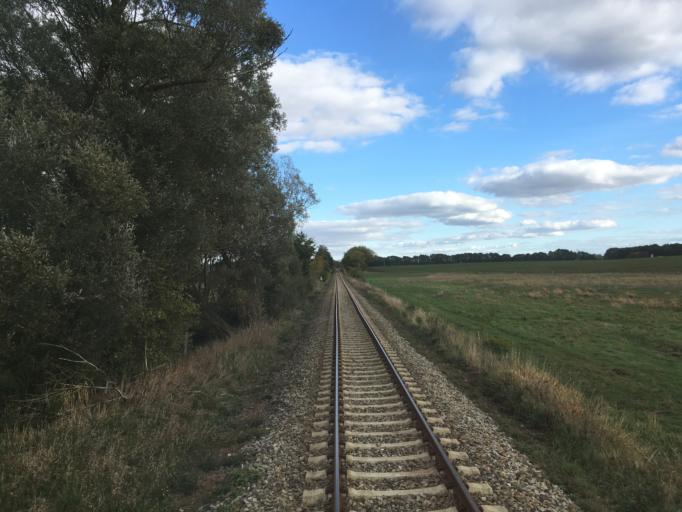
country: DE
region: Mecklenburg-Vorpommern
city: Grabowhofe
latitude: 53.5410
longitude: 12.5932
